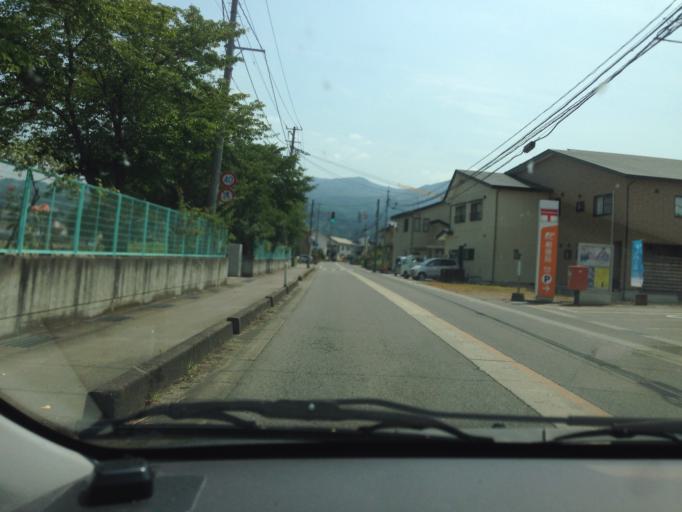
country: JP
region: Fukushima
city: Kitakata
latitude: 37.6428
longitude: 139.9224
